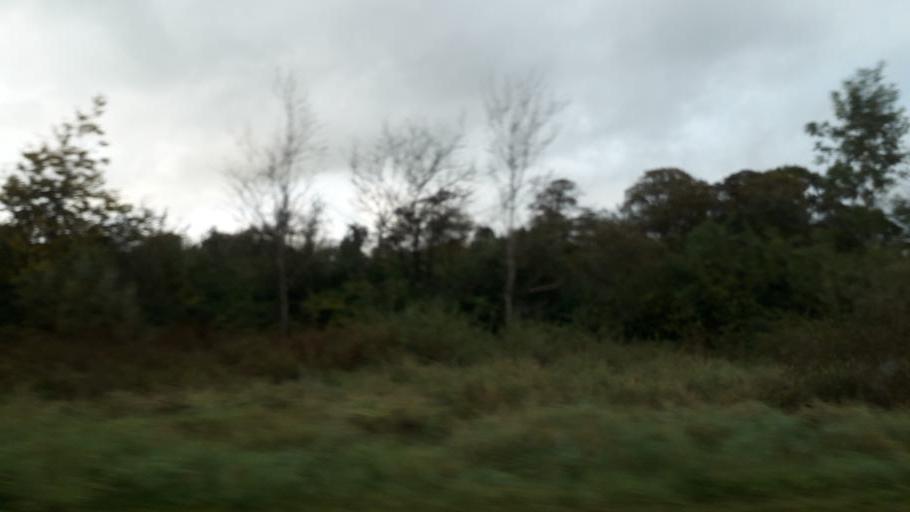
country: IE
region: Leinster
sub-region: An Longfort
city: Lanesborough
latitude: 53.7660
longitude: -8.0517
